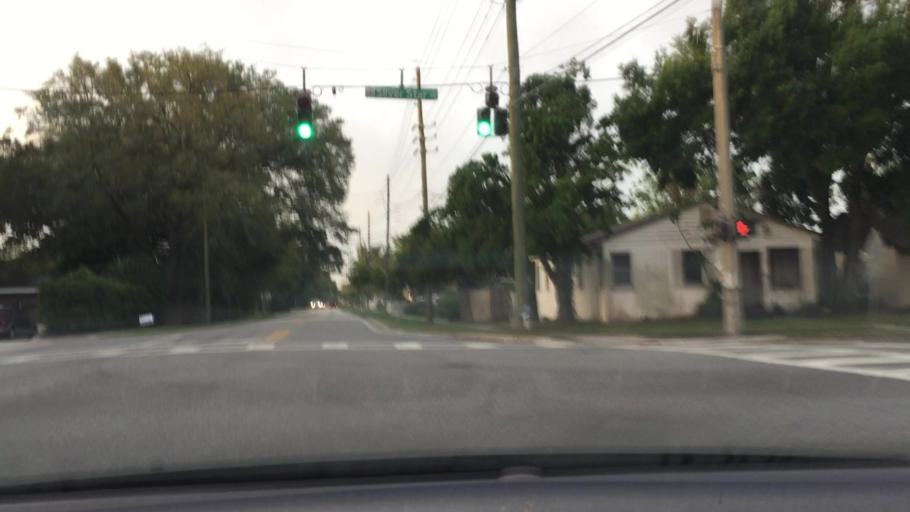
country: US
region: Florida
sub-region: Orange County
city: Fairview Shores
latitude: 28.5783
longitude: -81.4019
